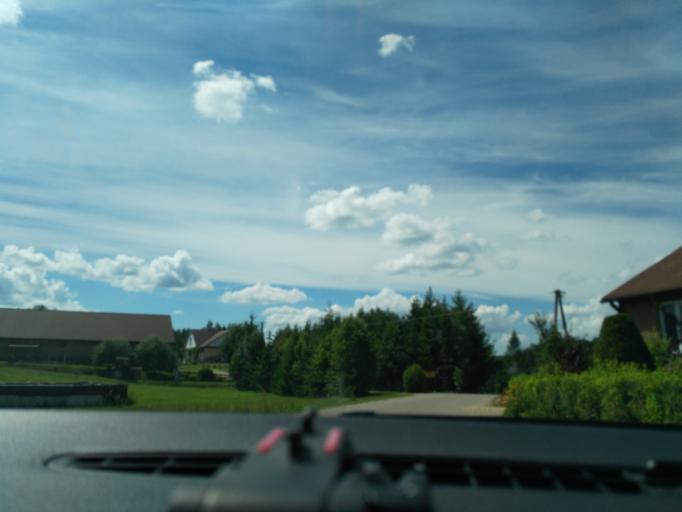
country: PL
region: Podlasie
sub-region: Powiat sejnenski
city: Sejny
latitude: 54.0303
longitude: 23.3229
